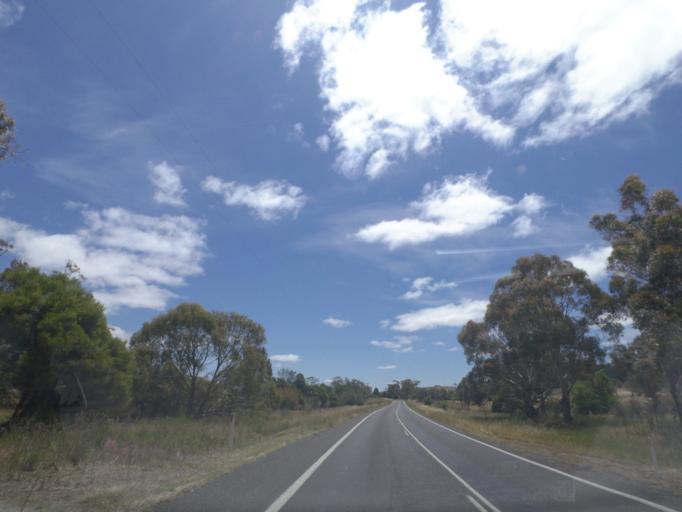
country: AU
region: Victoria
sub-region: Mount Alexander
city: Castlemaine
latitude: -37.2804
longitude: 144.1509
